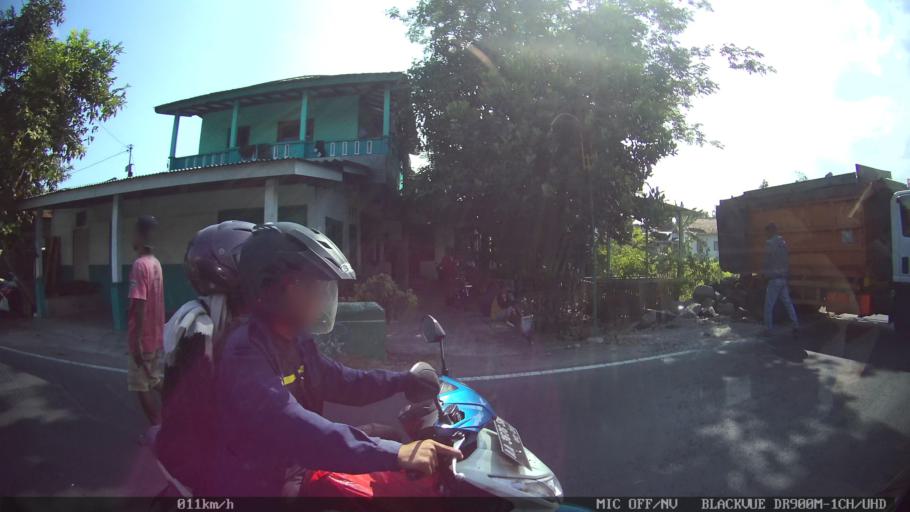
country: ID
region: Daerah Istimewa Yogyakarta
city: Sewon
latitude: -7.8731
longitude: 110.3917
